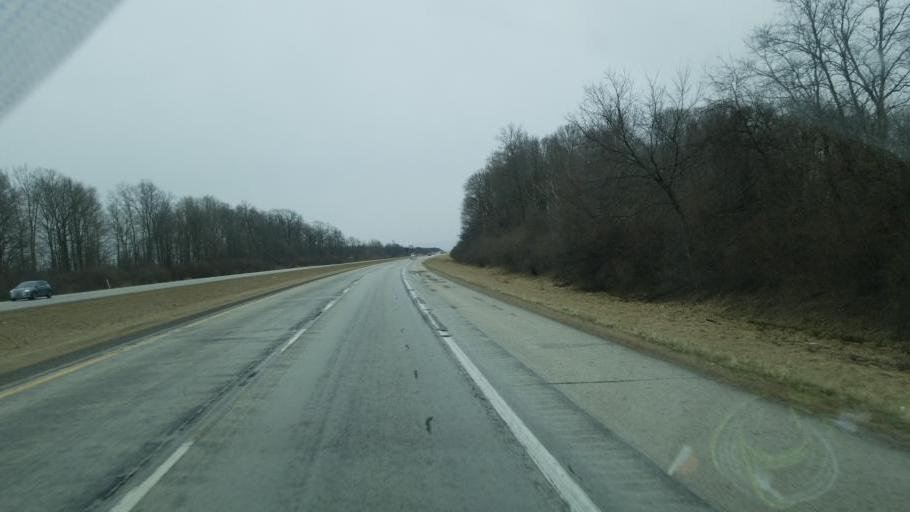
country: US
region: Indiana
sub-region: Marshall County
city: Argos
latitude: 41.1666
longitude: -86.2401
